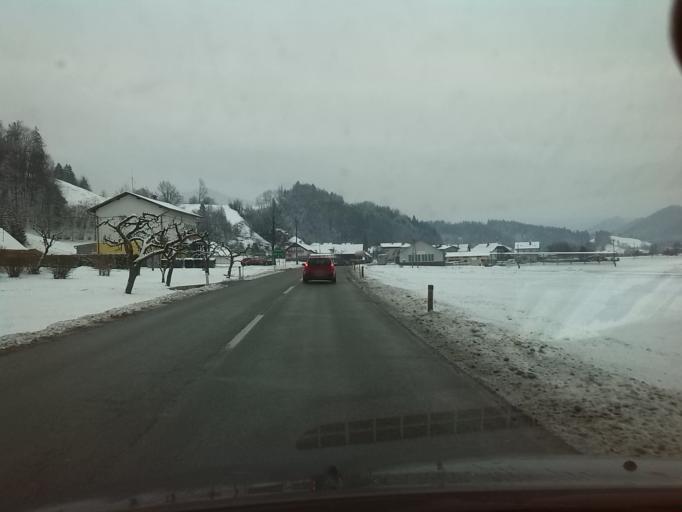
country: SI
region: Lukovica
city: Lukovica pri Domzalah
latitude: 46.2261
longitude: 14.6774
